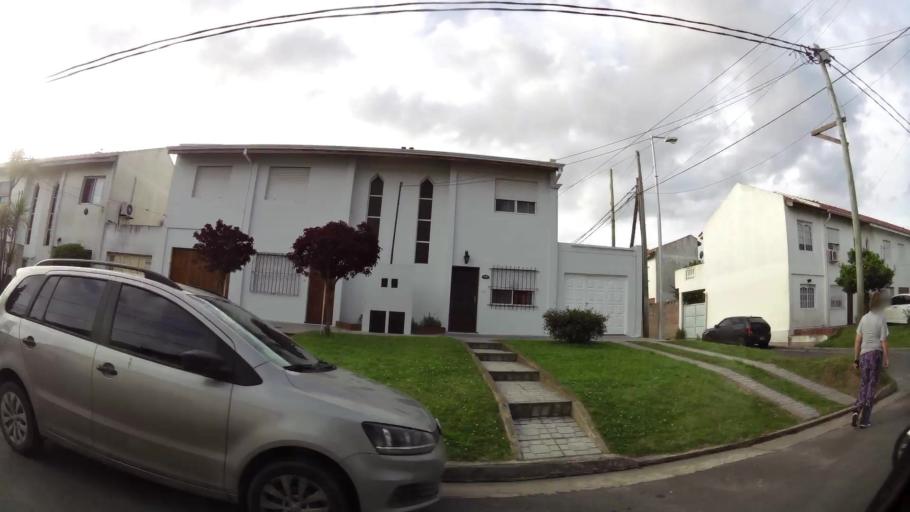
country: AR
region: Buenos Aires
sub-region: Partido de Quilmes
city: Quilmes
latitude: -34.7447
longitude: -58.2528
